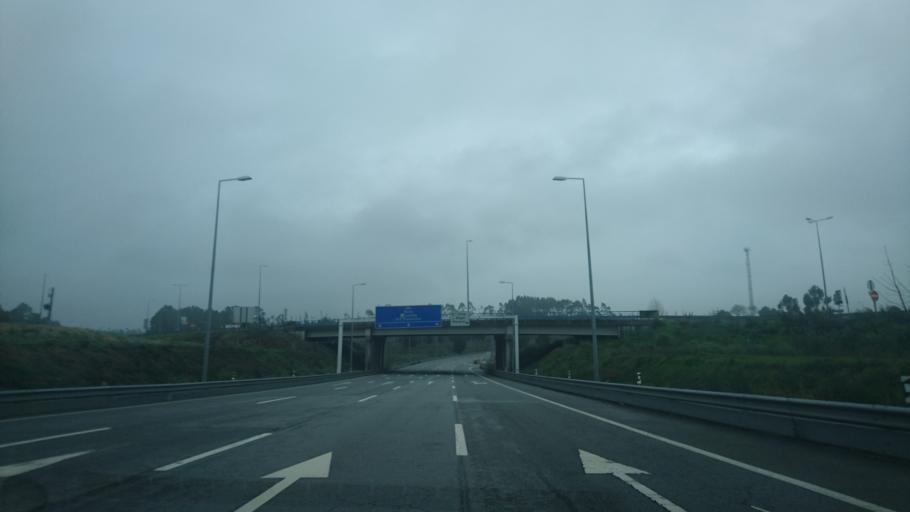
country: PT
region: Porto
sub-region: Matosinhos
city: Santa Cruz do Bispo
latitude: 41.2237
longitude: -8.6664
